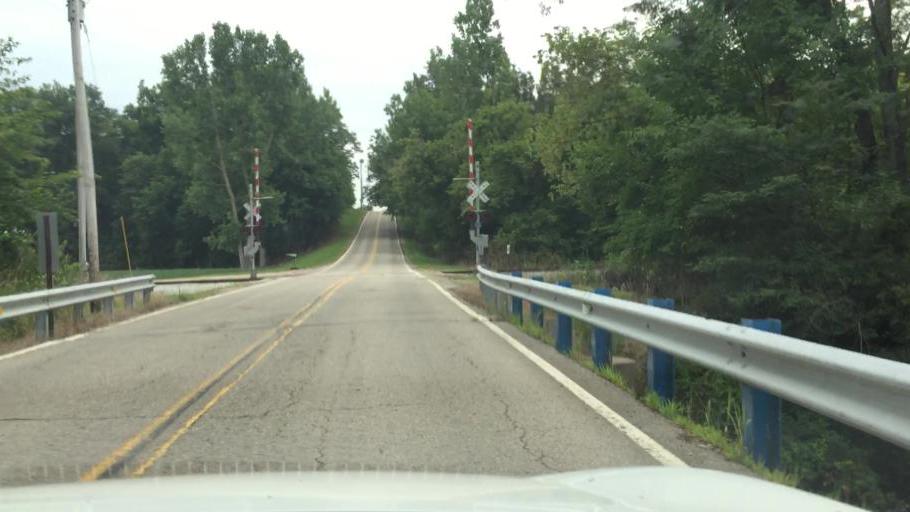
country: US
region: Ohio
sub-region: Clark County
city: Northridge
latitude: 40.0063
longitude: -83.6934
